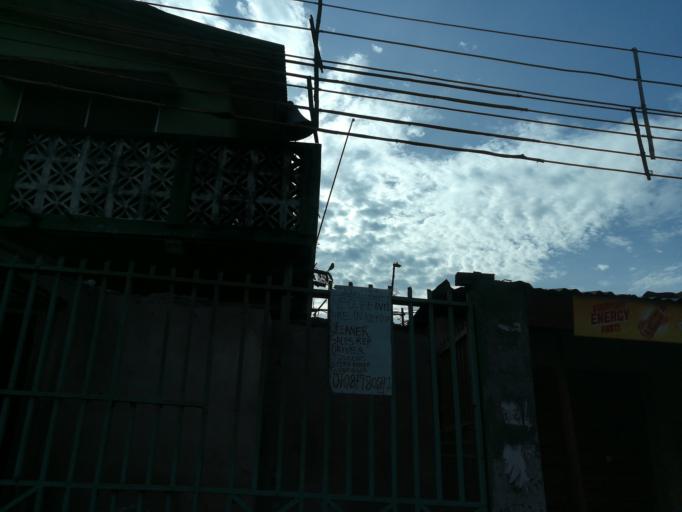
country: NG
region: Lagos
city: Oshodi
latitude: 6.5581
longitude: 3.3472
